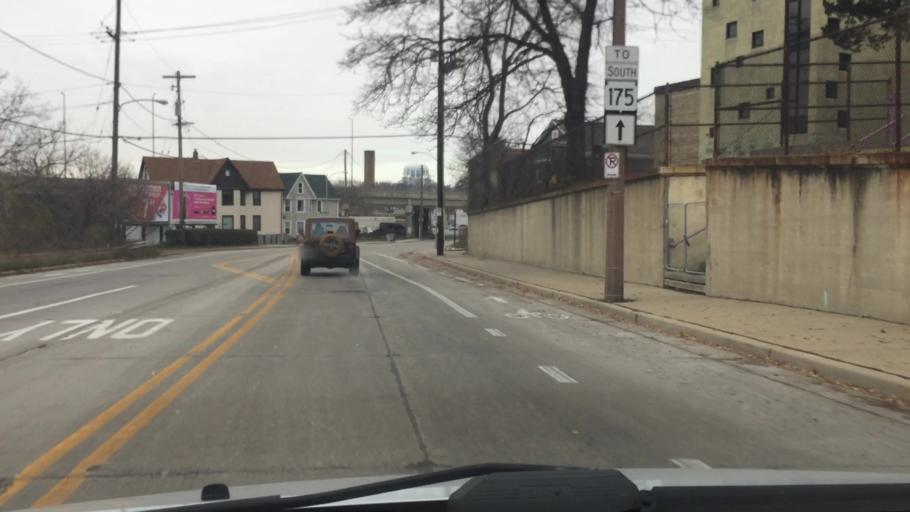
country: US
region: Wisconsin
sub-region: Milwaukee County
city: West Milwaukee
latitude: 43.0427
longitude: -87.9714
